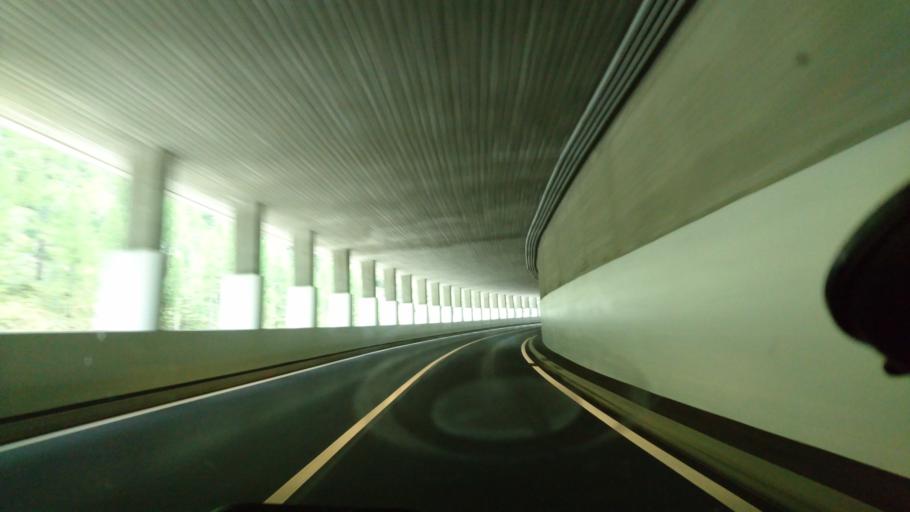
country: IT
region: Piedmont
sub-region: Provincia Verbano-Cusio-Ossola
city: San Lorenzo
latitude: 46.1857
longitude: 8.0885
